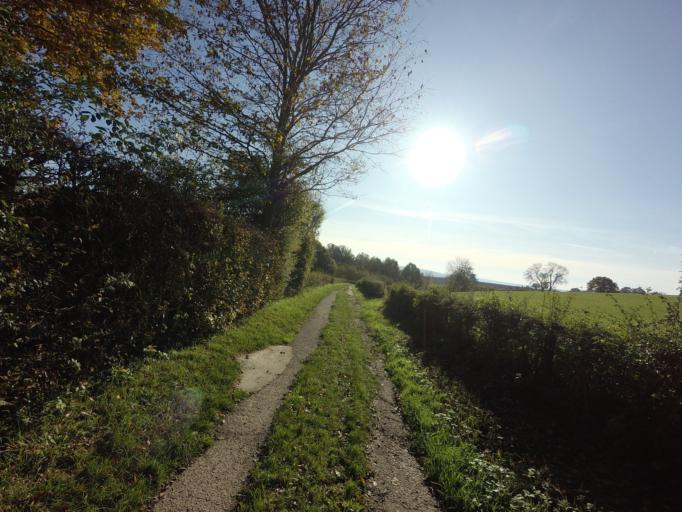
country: NL
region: Limburg
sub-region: Gemeente Voerendaal
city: Ubachsberg
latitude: 50.8381
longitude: 5.9514
